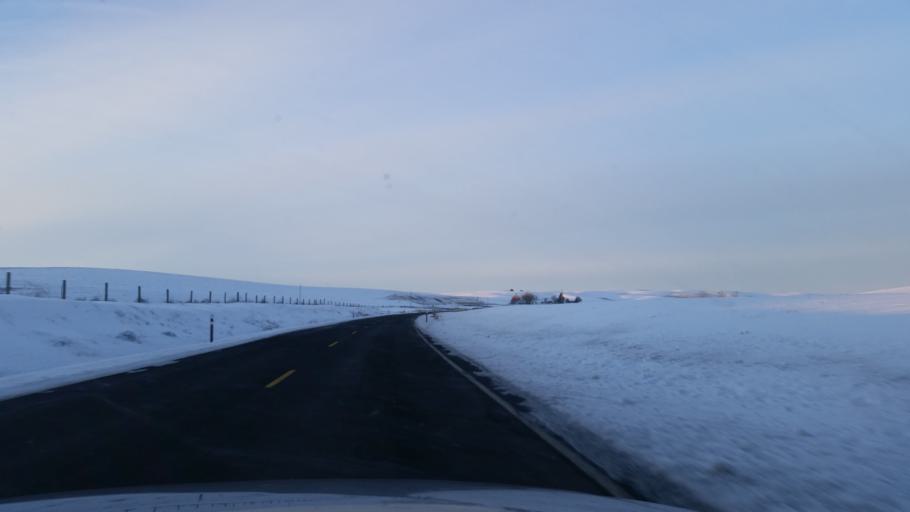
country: US
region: Washington
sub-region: Spokane County
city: Cheney
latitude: 47.1272
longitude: -117.8286
